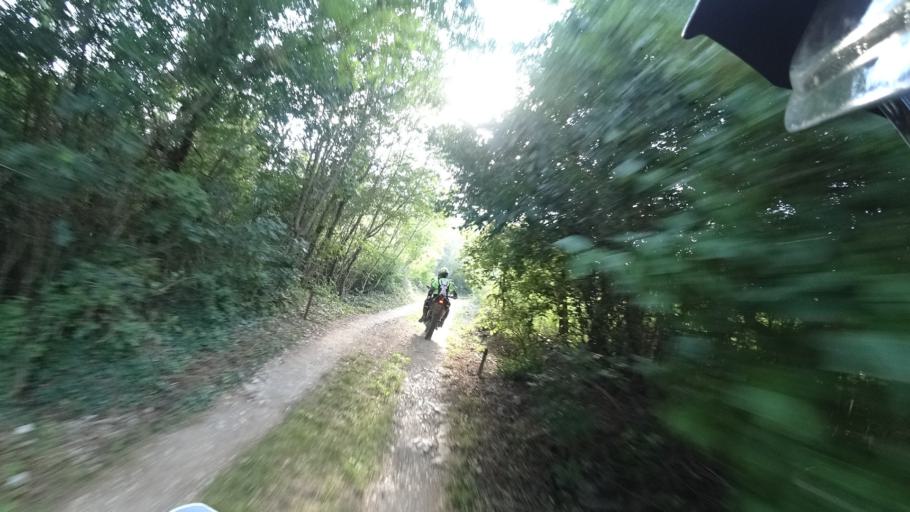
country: HR
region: Sibensko-Kniniska
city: Knin
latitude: 44.2035
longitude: 16.0720
